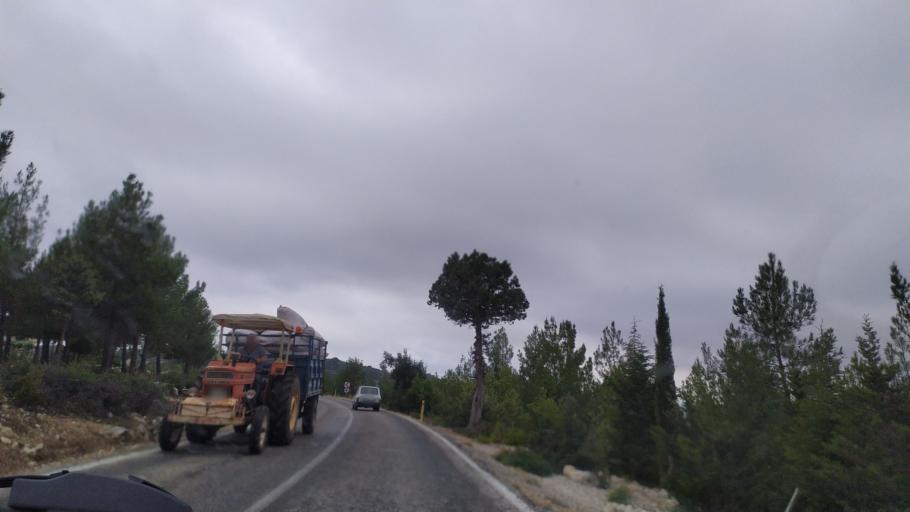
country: TR
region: Mersin
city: Silifke
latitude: 36.5451
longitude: 33.9264
